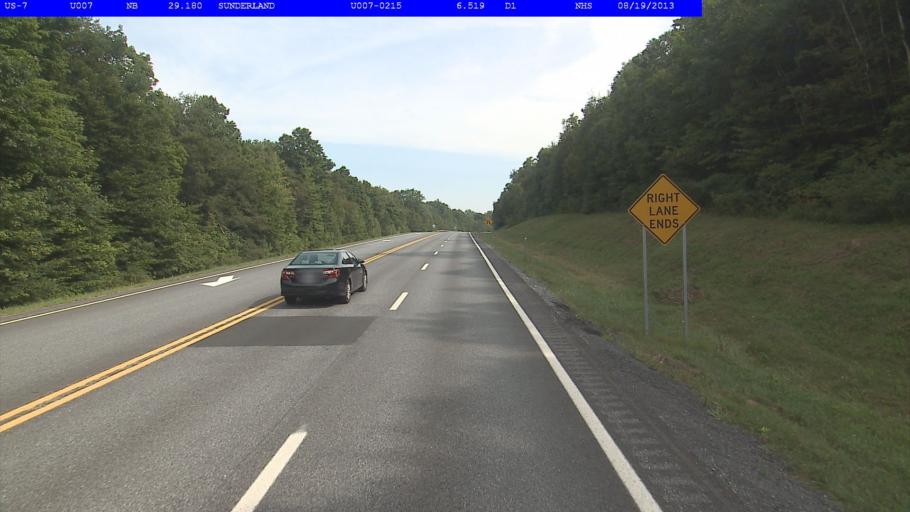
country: US
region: Vermont
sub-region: Bennington County
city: Manchester Center
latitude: 43.1108
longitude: -73.0886
